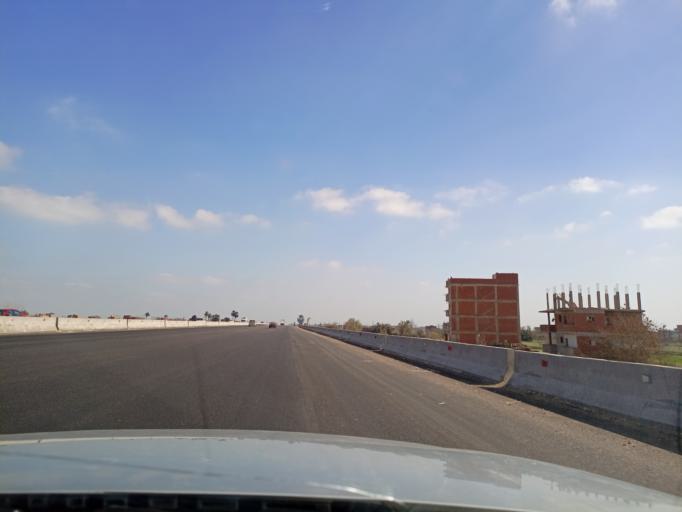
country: EG
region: Muhafazat al Minufiyah
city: Al Bajur
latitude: 30.4104
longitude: 31.0554
